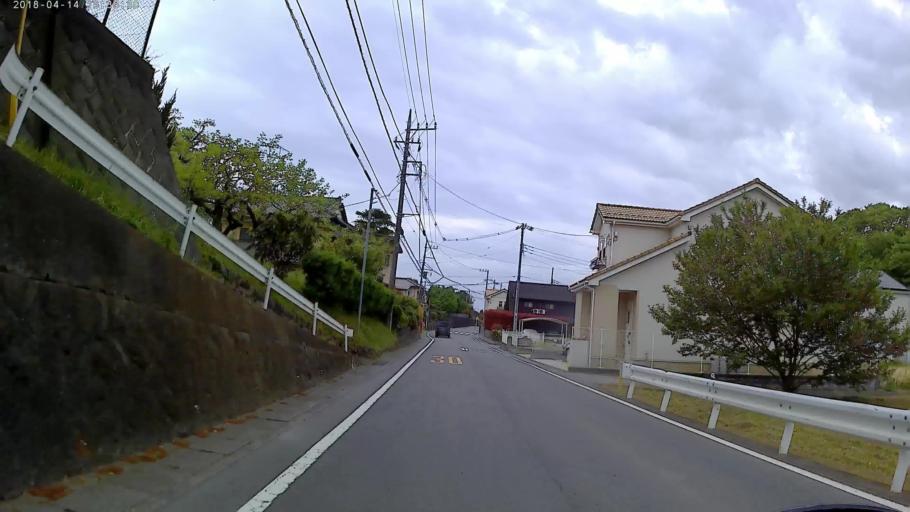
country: JP
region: Kanagawa
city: Hadano
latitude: 35.3357
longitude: 139.1618
